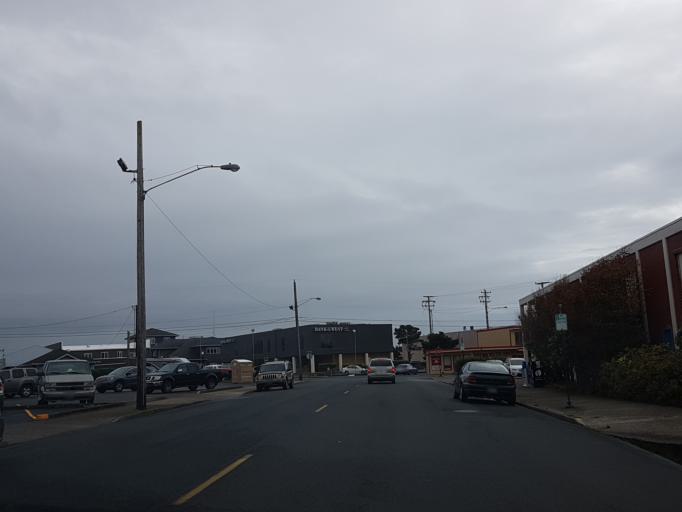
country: US
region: Oregon
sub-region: Lincoln County
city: Newport
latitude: 44.6355
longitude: -124.0557
